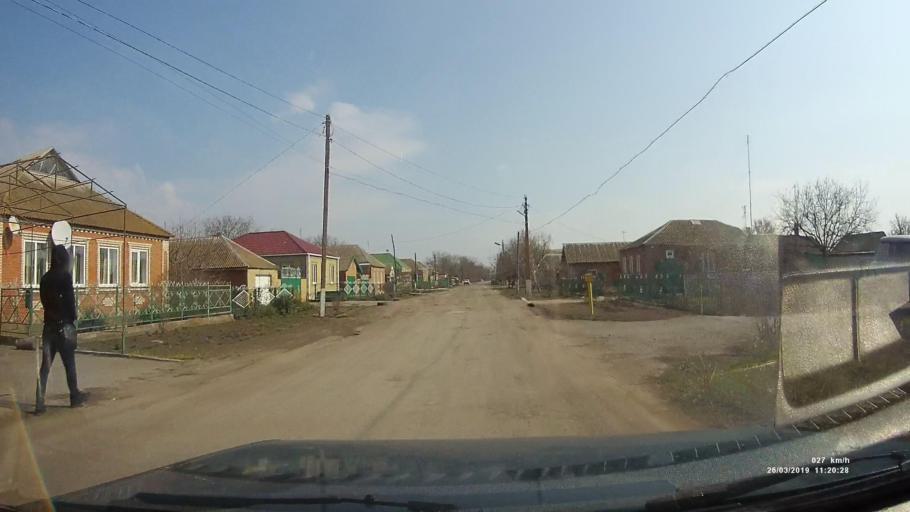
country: RU
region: Krasnodarskiy
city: Shabel'skoye
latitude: 47.1367
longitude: 38.5452
